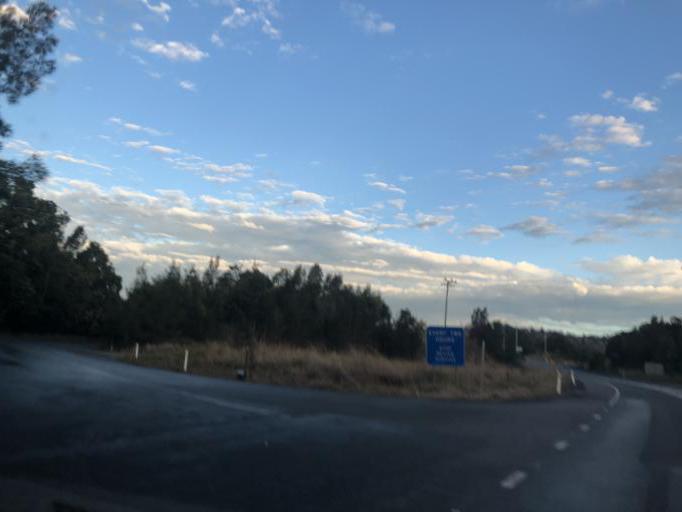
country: AU
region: New South Wales
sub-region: Nambucca Shire
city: Macksville
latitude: -30.7303
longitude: 152.9188
